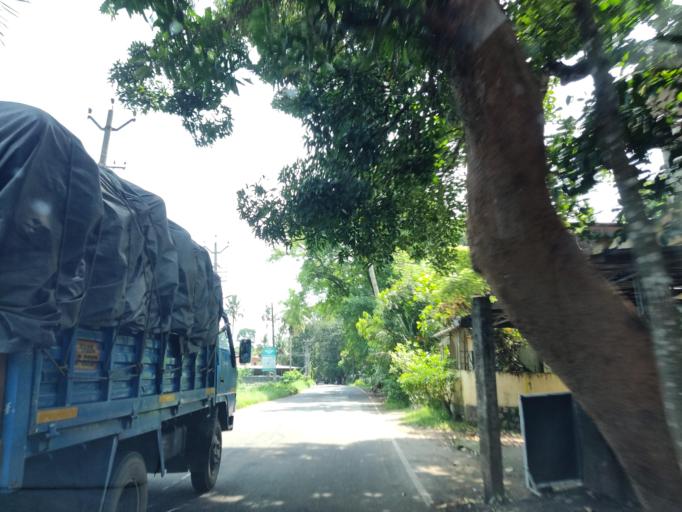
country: IN
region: Kerala
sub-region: Alappuzha
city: Chengannur
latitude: 9.3083
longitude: 76.5748
